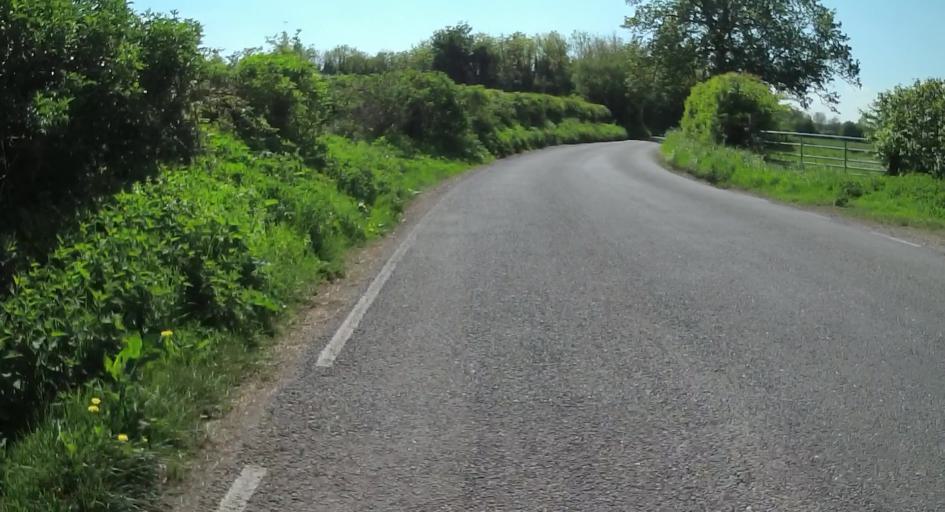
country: GB
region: England
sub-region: Hampshire
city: Andover
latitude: 51.1622
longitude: -1.4340
